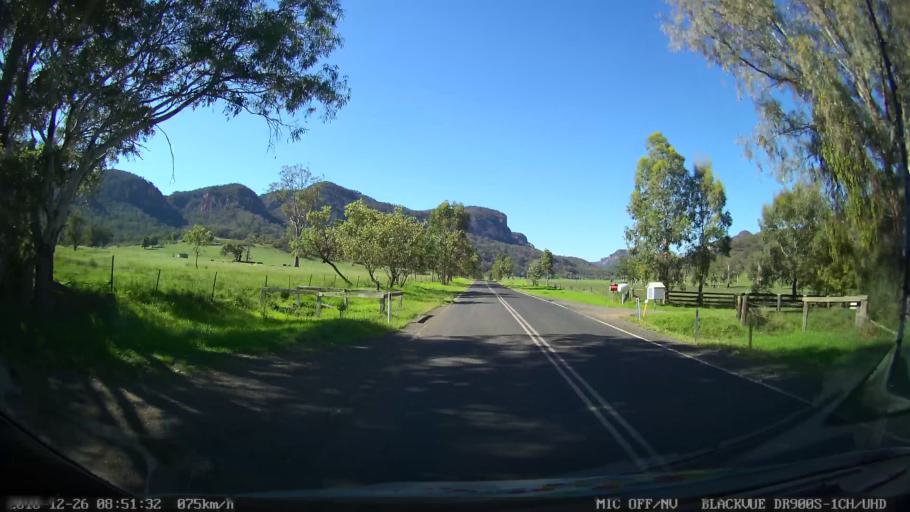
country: AU
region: New South Wales
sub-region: Mid-Western Regional
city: Kandos
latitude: -32.5864
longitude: 150.0885
